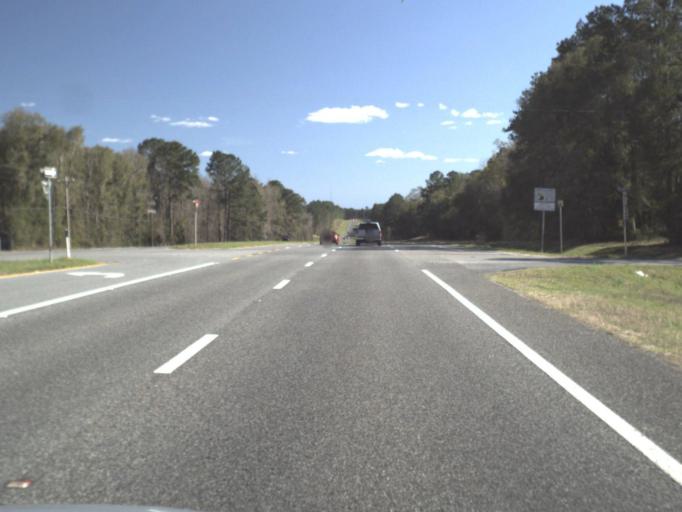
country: US
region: Florida
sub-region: Gadsden County
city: Midway
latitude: 30.5355
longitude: -84.4757
